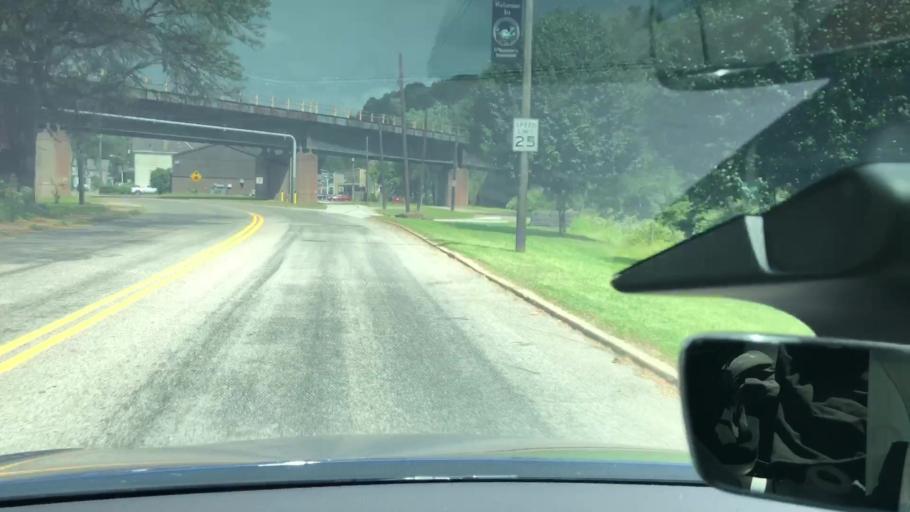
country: US
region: Pennsylvania
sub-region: Allegheny County
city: Turtle Creek
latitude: 40.4074
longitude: -79.8263
